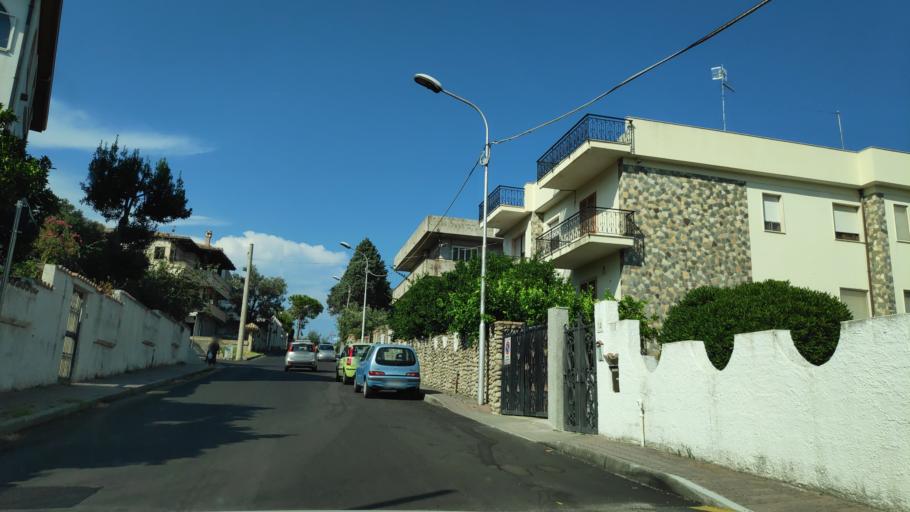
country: IT
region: Calabria
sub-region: Provincia di Catanzaro
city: Martelli-Laganosa
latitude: 38.6807
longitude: 16.5427
